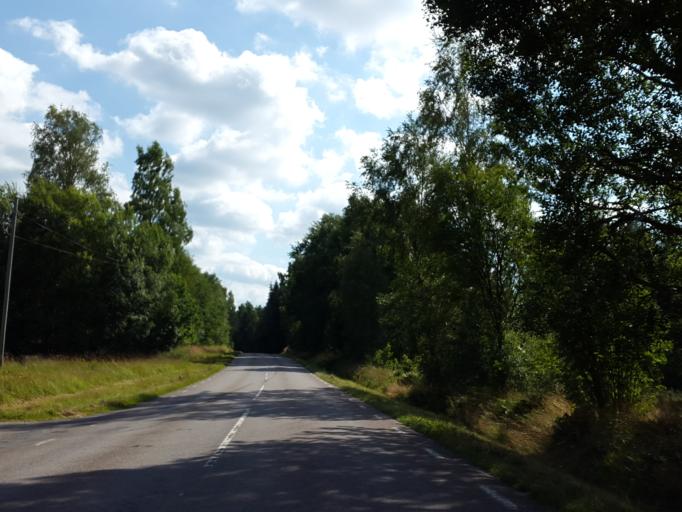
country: SE
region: Vaestra Goetaland
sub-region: Herrljunga Kommun
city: Herrljunga
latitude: 58.0447
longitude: 13.0989
